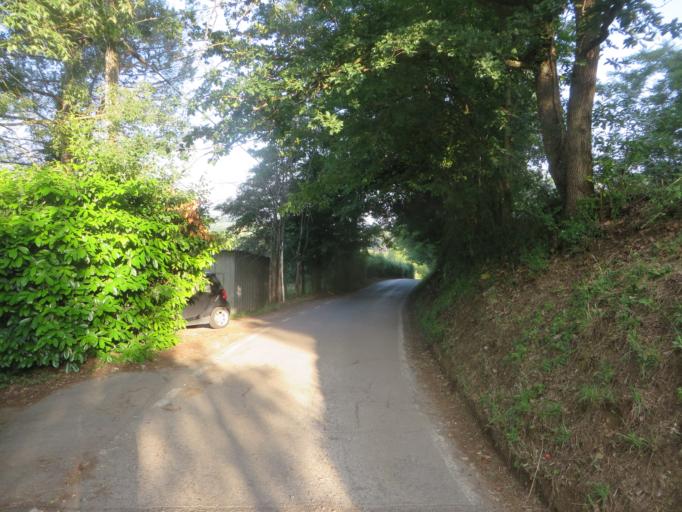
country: IT
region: Tuscany
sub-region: Province of Florence
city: Bagno a Ripoli
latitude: 43.7482
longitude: 11.3210
